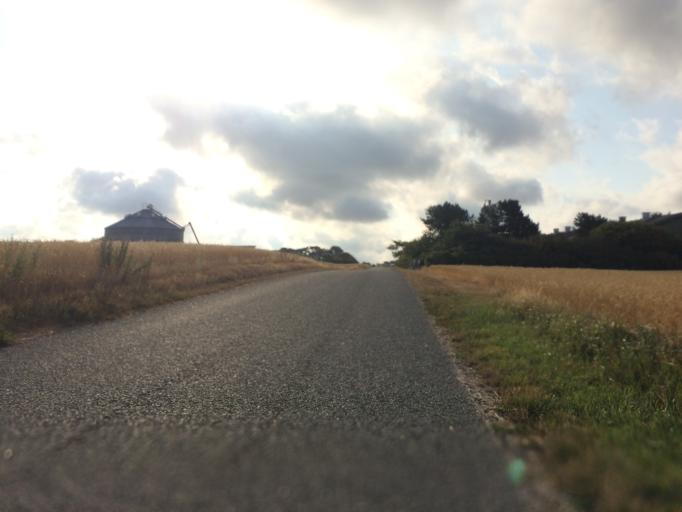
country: DK
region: Central Jutland
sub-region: Holstebro Kommune
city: Vinderup
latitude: 56.6194
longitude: 8.7470
